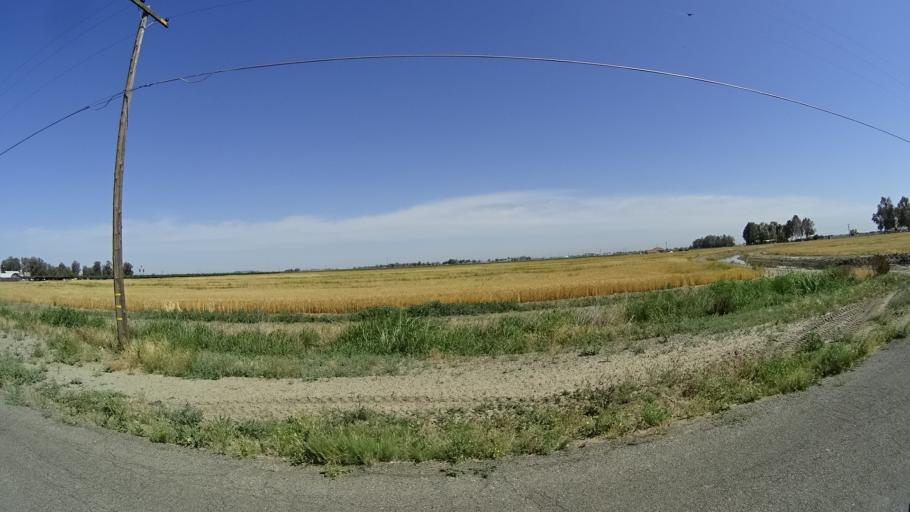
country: US
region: California
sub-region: Kings County
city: Stratford
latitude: 36.1967
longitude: -119.7832
